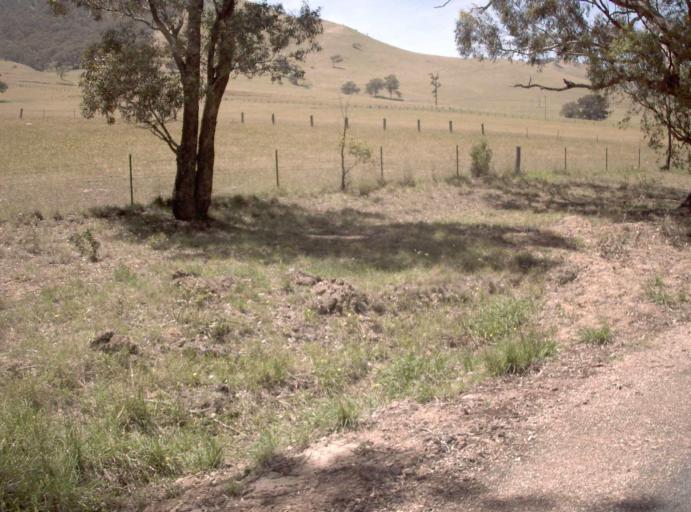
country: AU
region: Victoria
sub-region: East Gippsland
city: Bairnsdale
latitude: -37.3364
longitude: 147.7870
